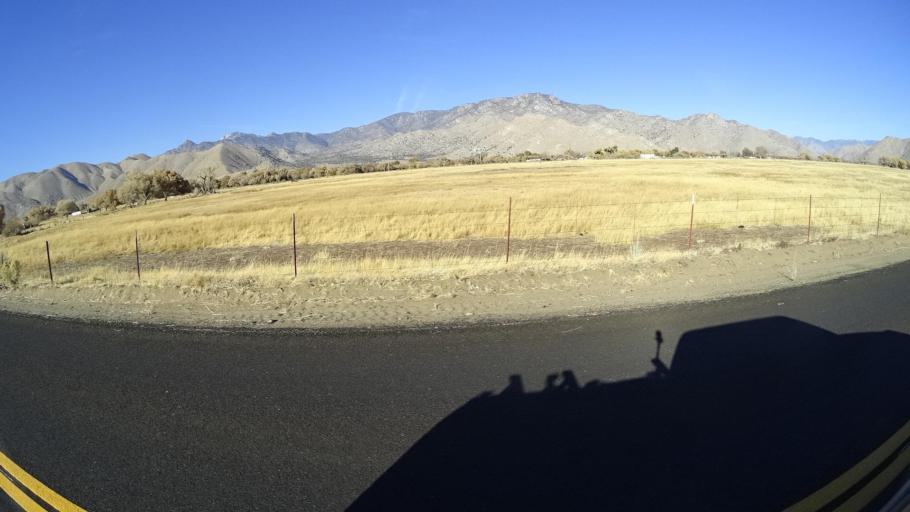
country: US
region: California
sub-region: Kern County
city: Weldon
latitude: 35.6615
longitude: -118.2984
